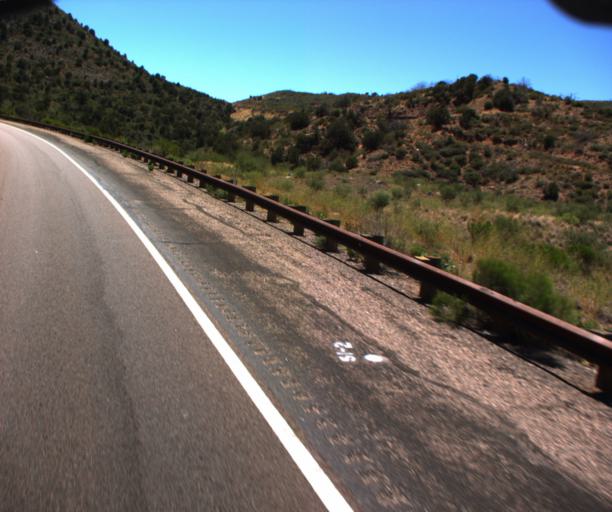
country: US
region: Arizona
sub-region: Gila County
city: Tonto Basin
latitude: 33.9463
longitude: -111.4406
